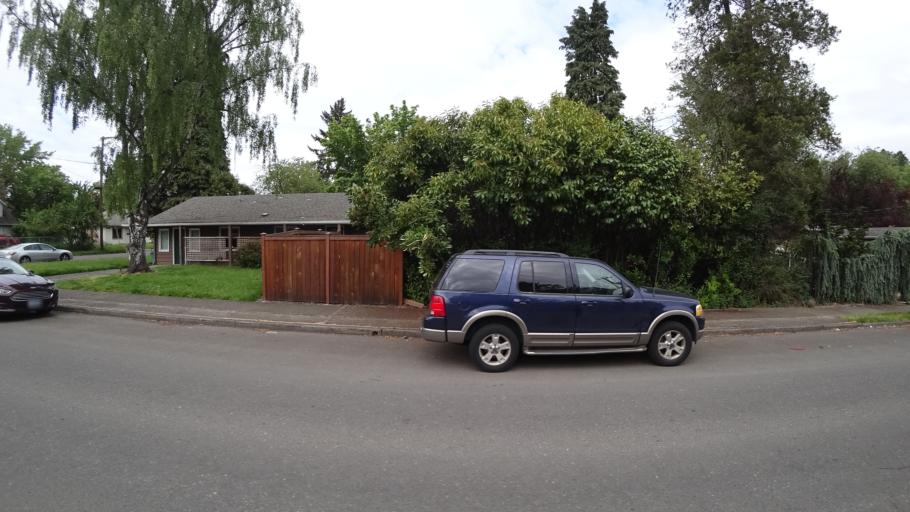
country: US
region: Oregon
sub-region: Washington County
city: Beaverton
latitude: 45.4823
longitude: -122.8050
